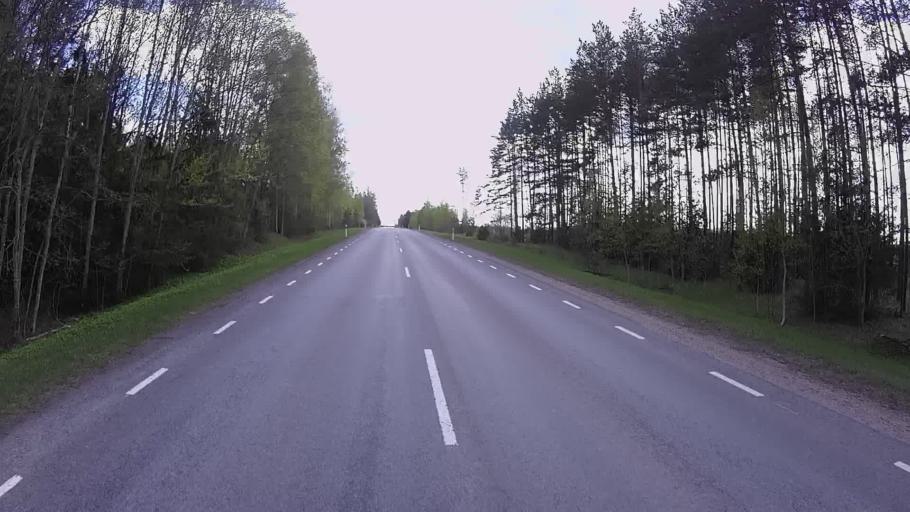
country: EE
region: Tartu
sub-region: Alatskivi vald
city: Kallaste
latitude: 58.5247
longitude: 27.0069
